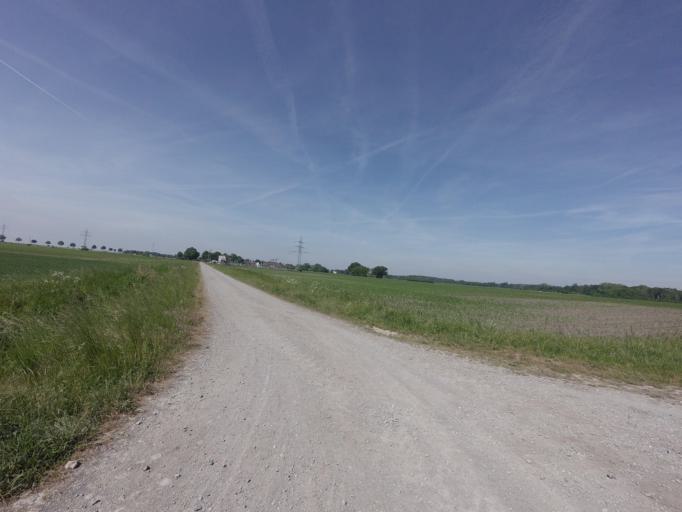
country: DE
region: Lower Saxony
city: Vordorf
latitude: 52.3791
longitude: 10.4976
